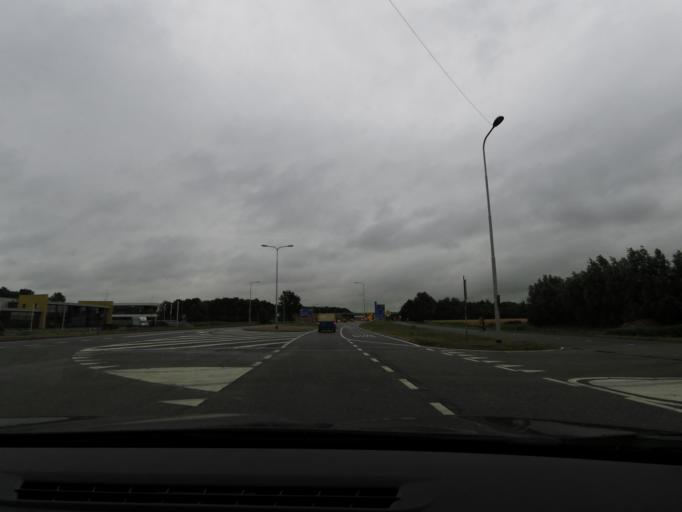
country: NL
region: South Holland
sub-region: Gemeente Brielle
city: Brielle
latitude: 51.8923
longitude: 4.1931
